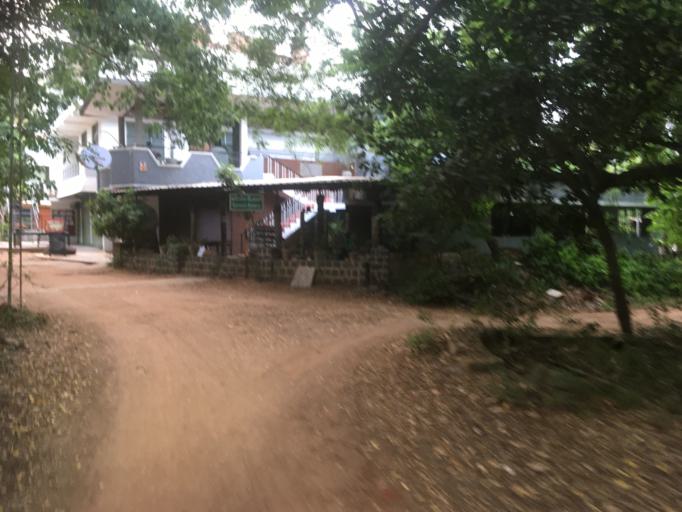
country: IN
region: Tamil Nadu
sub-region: Villupuram
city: Auroville
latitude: 12.0149
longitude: 79.8022
